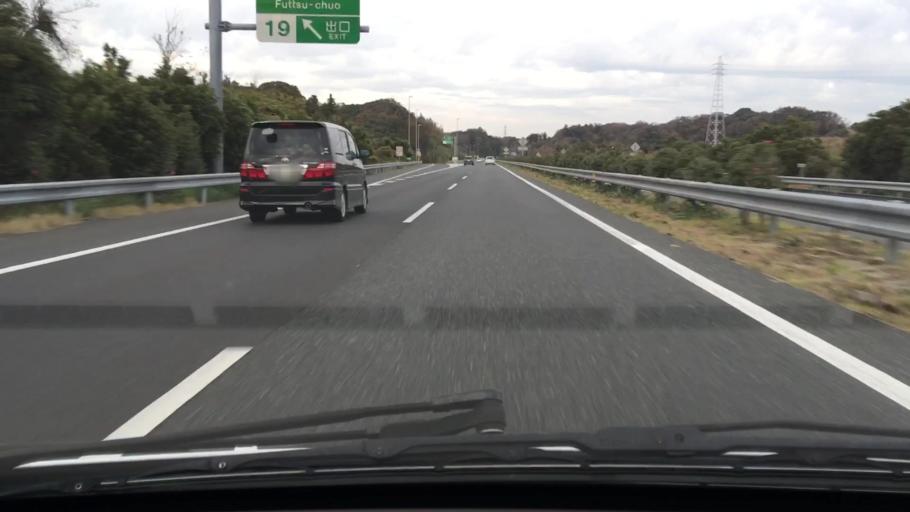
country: JP
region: Chiba
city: Kimitsu
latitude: 35.2476
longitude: 139.8906
